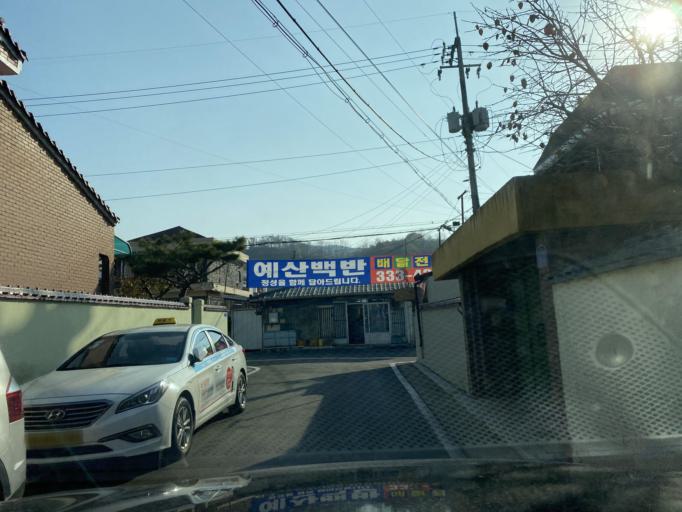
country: KR
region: Chungcheongnam-do
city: Yesan
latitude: 36.6777
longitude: 126.8443
